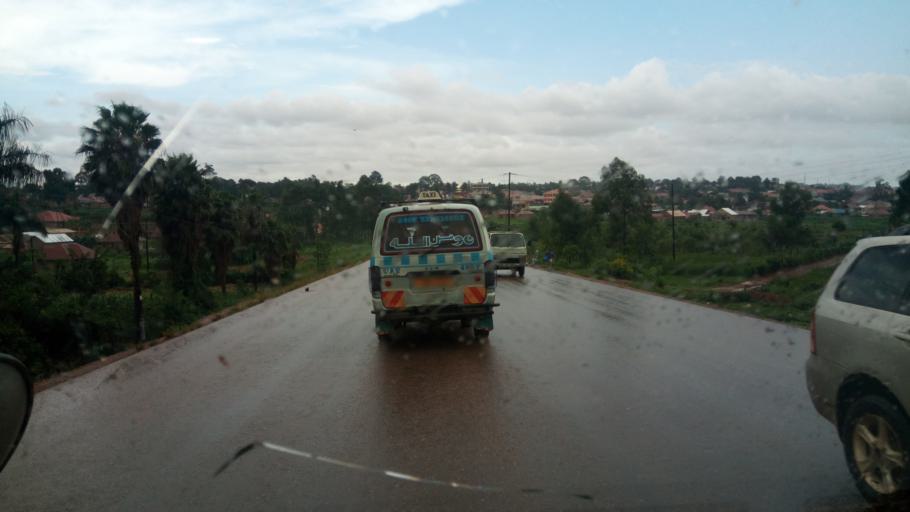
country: UG
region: Central Region
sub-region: Wakiso District
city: Wakiso
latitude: 0.3886
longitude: 32.5102
